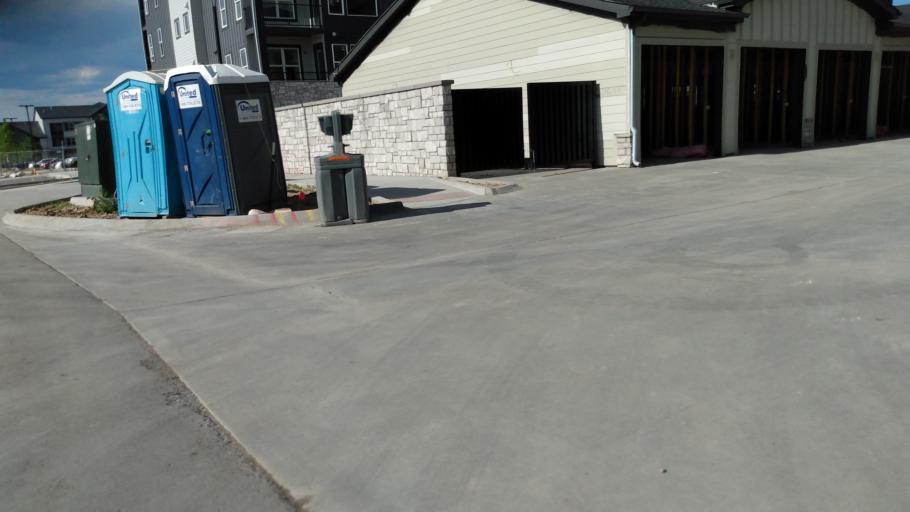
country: US
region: Colorado
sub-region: Boulder County
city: Lafayette
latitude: 40.0126
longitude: -105.0992
